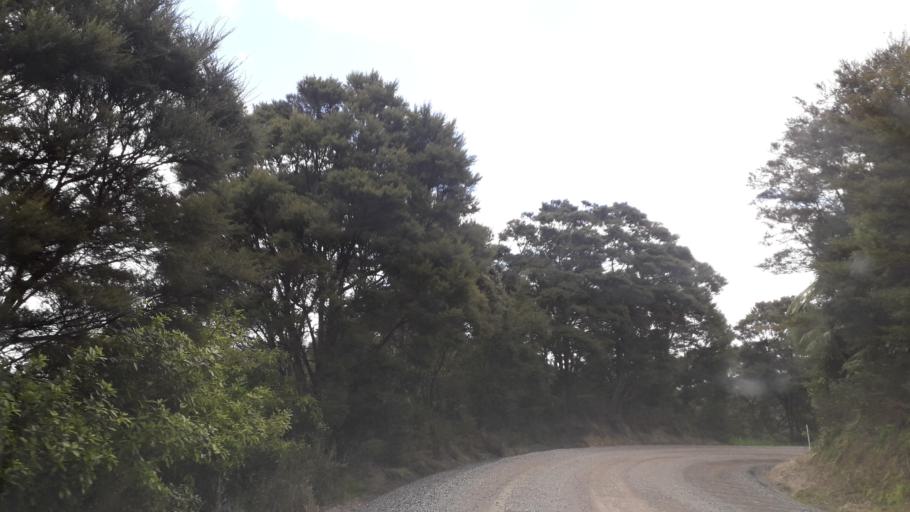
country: NZ
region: Northland
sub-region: Far North District
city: Paihia
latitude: -35.3177
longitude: 174.2307
